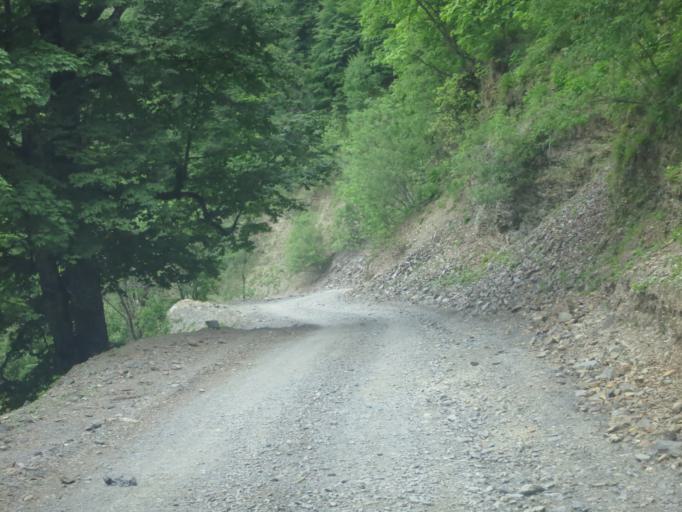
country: GE
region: Kakheti
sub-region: Telavi
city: Telavi
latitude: 42.2497
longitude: 45.4983
